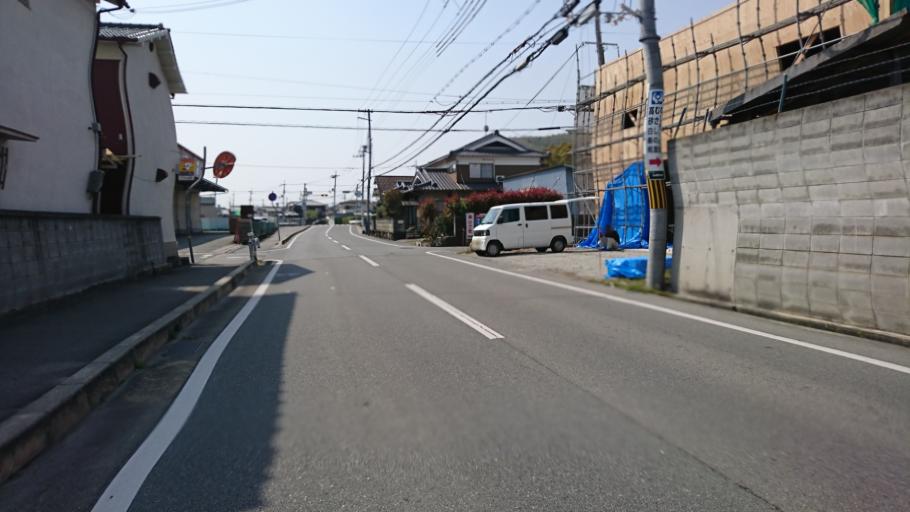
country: JP
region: Hyogo
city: Shirahamacho-usazakiminami
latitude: 34.7863
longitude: 134.7510
